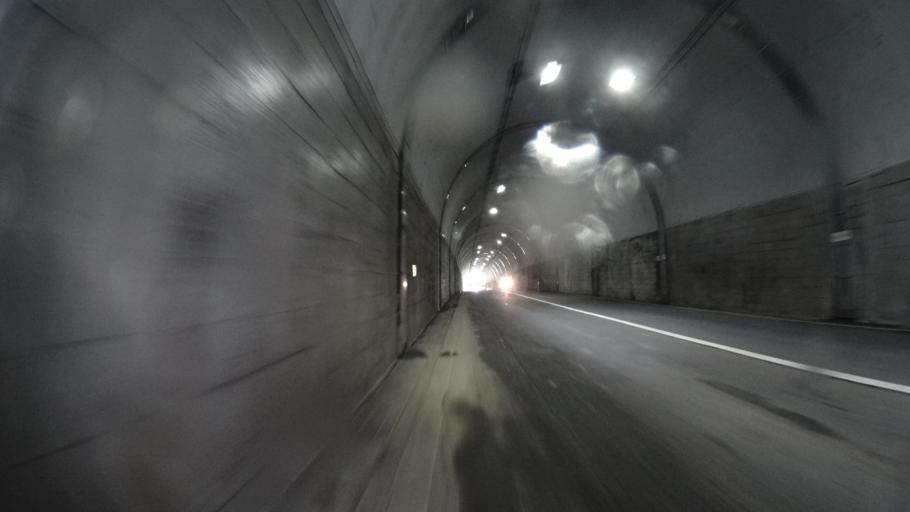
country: JP
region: Yamanashi
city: Uenohara
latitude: 35.7838
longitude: 139.0316
